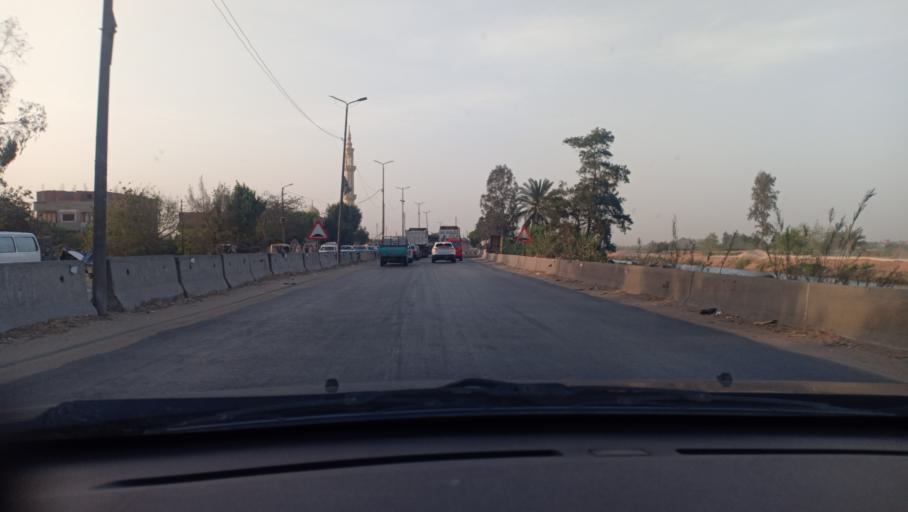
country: EG
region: Muhafazat al Minufiyah
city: Quwaysina
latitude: 30.5886
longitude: 31.2736
